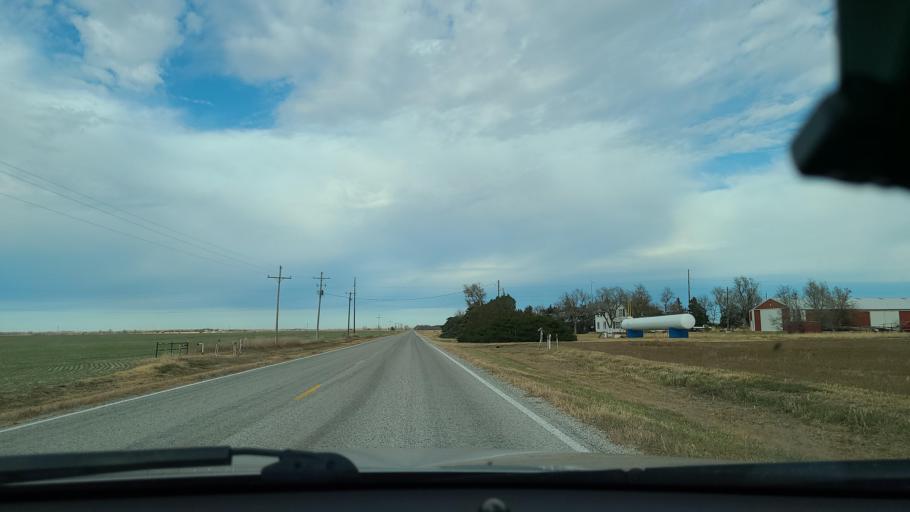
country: US
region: Kansas
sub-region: McPherson County
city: Inman
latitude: 38.3680
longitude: -97.9243
